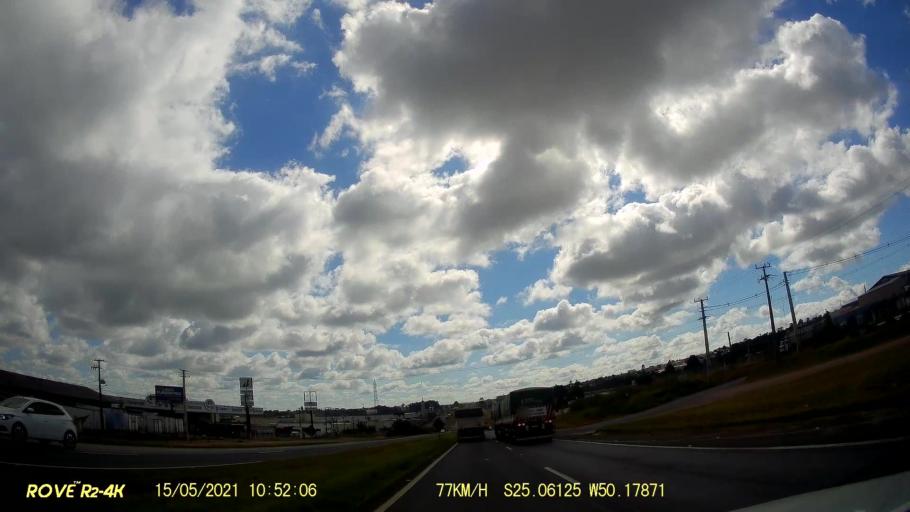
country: BR
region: Parana
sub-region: Ponta Grossa
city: Ponta Grossa
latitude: -25.0615
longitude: -50.1787
